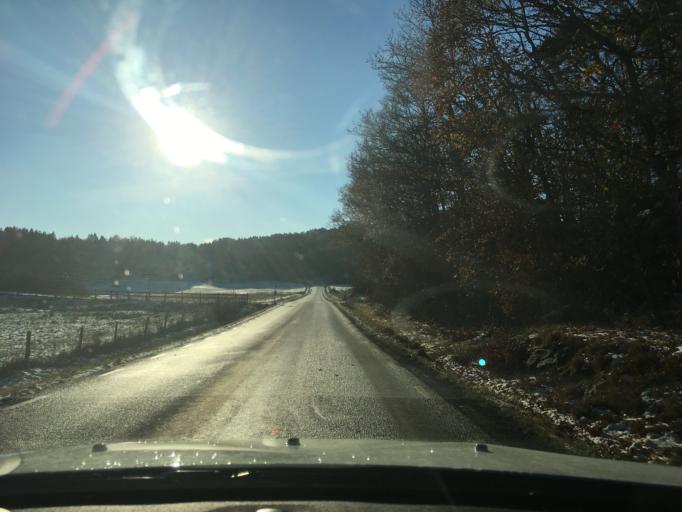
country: SE
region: Vaestra Goetaland
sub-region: Tjorns Kommun
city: Myggenas
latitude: 58.0550
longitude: 11.6761
